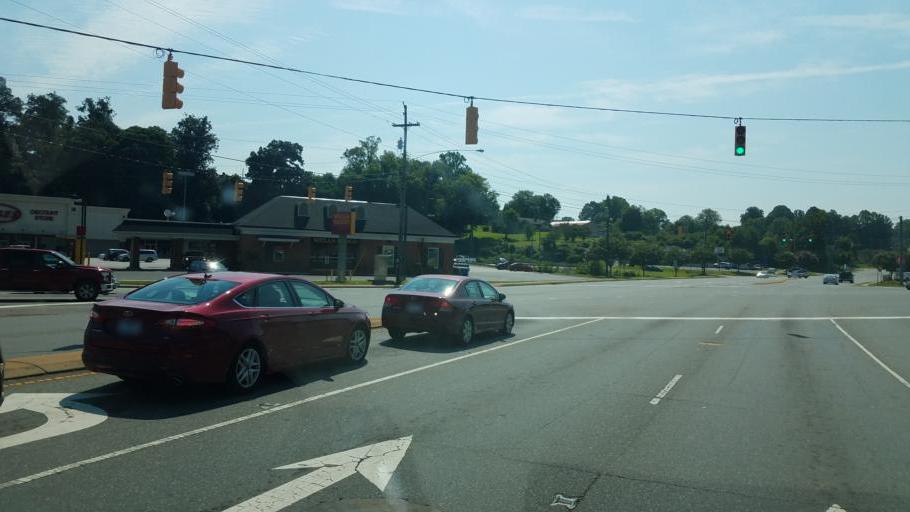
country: US
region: North Carolina
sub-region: Burke County
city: Morganton
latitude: 35.7399
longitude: -81.6804
